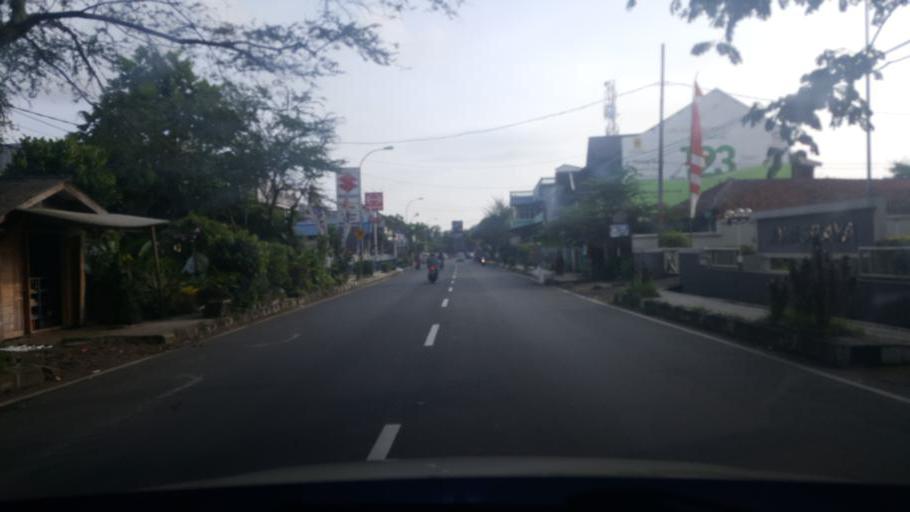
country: ID
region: West Java
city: Cibogor
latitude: -7.3177
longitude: 108.2280
